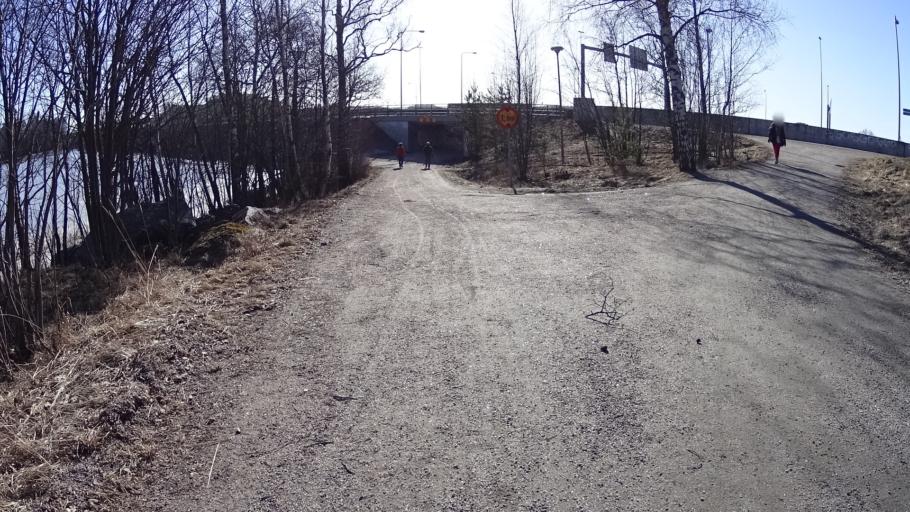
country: FI
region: Uusimaa
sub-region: Helsinki
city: Otaniemi
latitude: 60.1705
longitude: 24.8147
